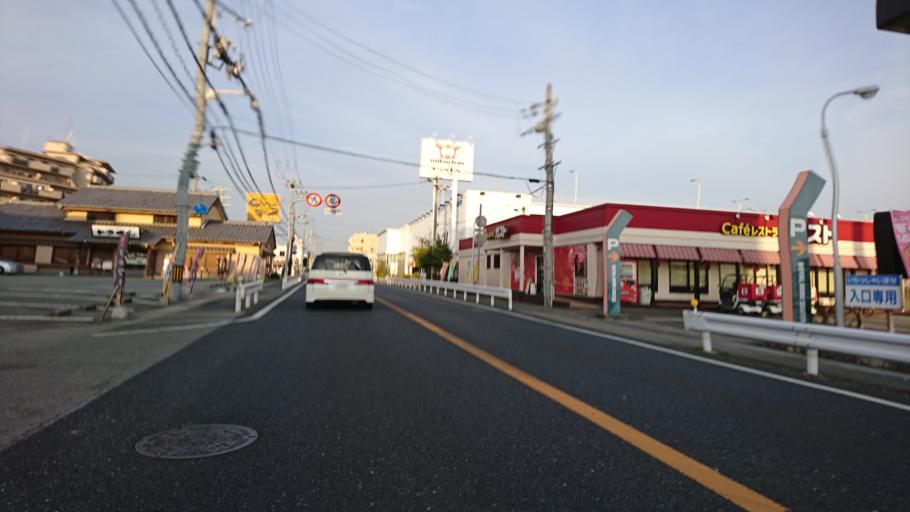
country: JP
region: Hyogo
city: Kakogawacho-honmachi
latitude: 34.7391
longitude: 134.8564
